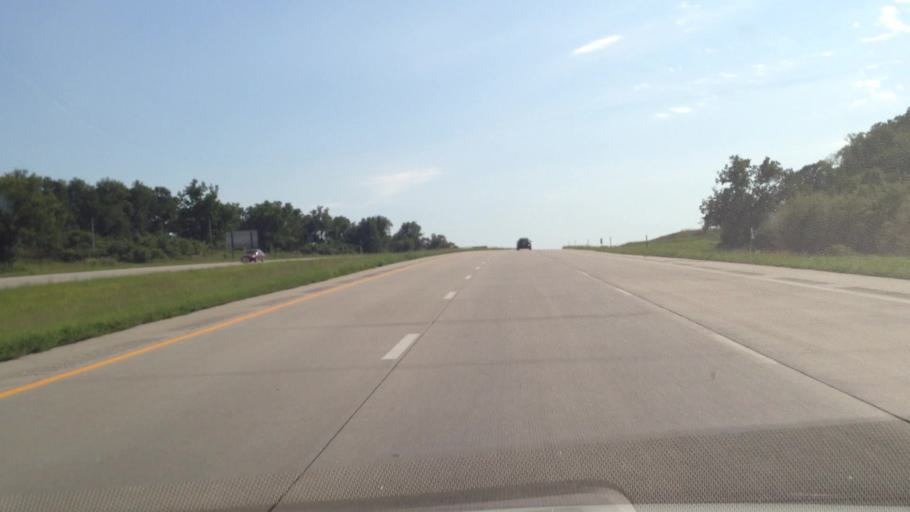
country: US
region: Kansas
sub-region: Linn County
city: Pleasanton
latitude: 38.2599
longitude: -94.6744
